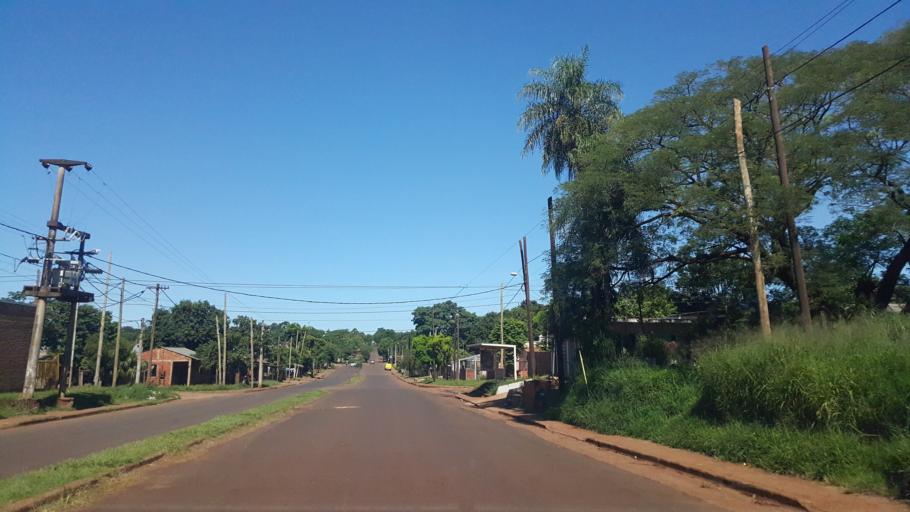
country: AR
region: Misiones
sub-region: Departamento de Capital
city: Posadas
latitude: -27.3880
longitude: -55.9277
